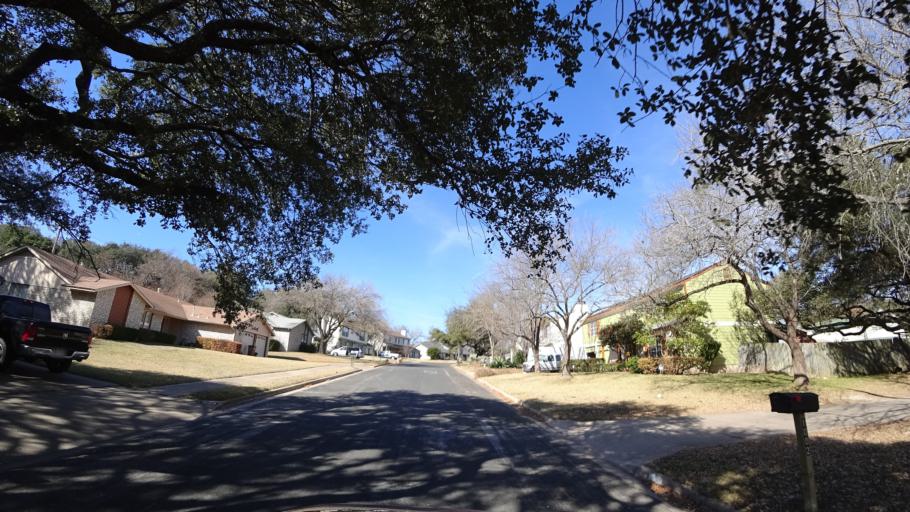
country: US
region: Texas
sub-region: Travis County
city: Wells Branch
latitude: 30.3888
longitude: -97.6875
